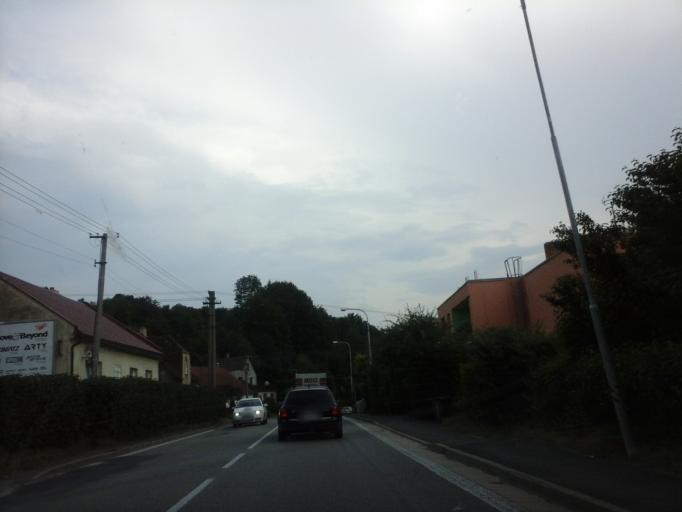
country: CZ
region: Pardubicky
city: Brnenec
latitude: 49.6188
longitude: 16.5308
